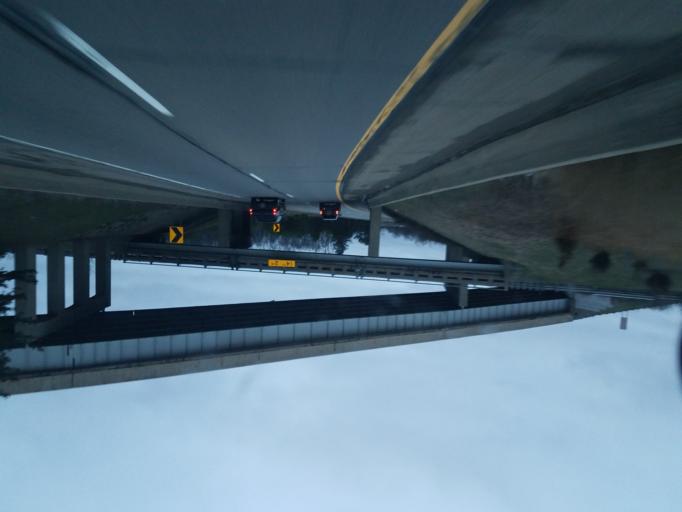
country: US
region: Michigan
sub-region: Washtenaw County
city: Ann Arbor
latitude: 42.3221
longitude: -83.6895
